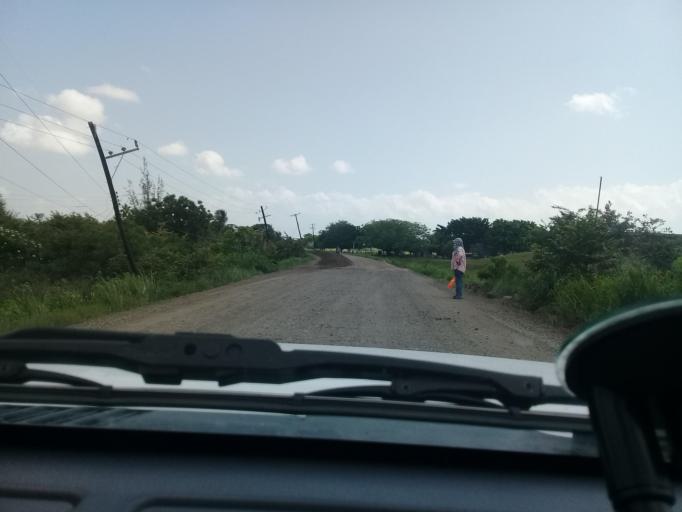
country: MX
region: Veracruz
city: Moralillo
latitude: 22.1791
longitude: -97.9477
